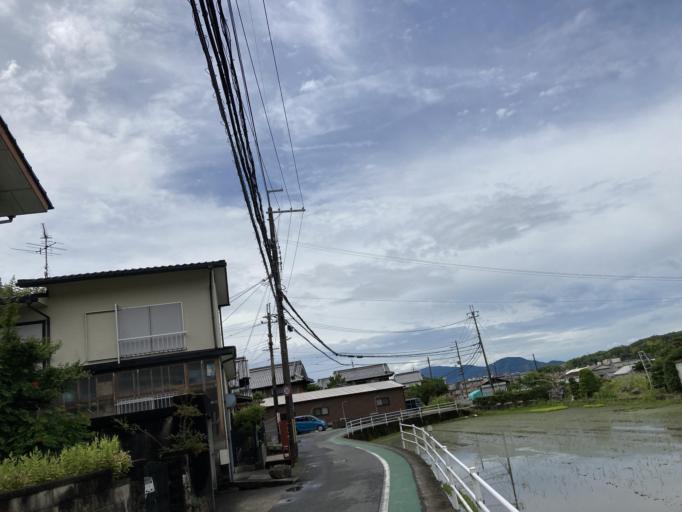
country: JP
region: Nara
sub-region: Ikoma-shi
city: Ikoma
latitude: 34.6210
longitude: 135.7089
